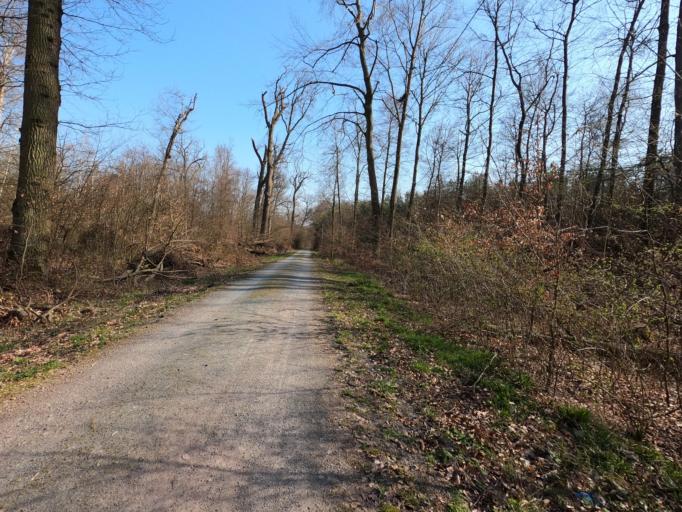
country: DE
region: Hesse
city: Morfelden-Walldorf
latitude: 49.9609
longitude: 8.5534
